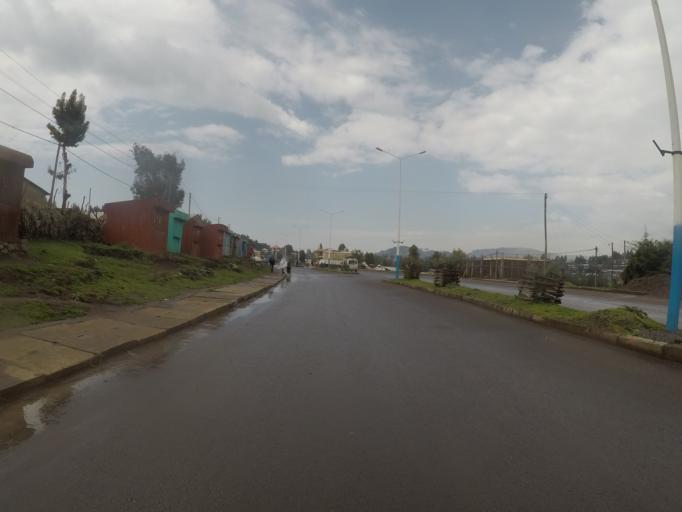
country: ET
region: Amhara
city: Debark'
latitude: 13.1456
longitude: 37.8943
